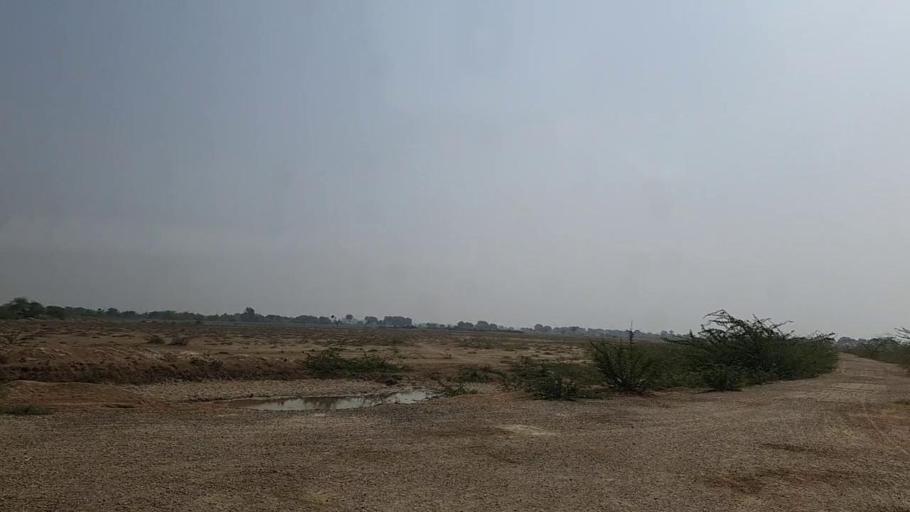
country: PK
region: Sindh
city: Naukot
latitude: 24.8098
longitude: 69.3615
